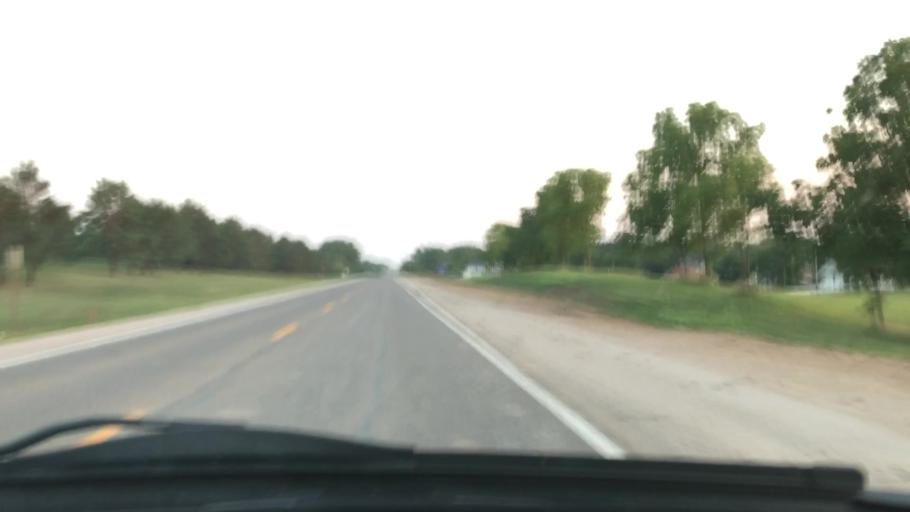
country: US
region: Iowa
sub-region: Henry County
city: Mount Pleasant
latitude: 40.9582
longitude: -91.5394
